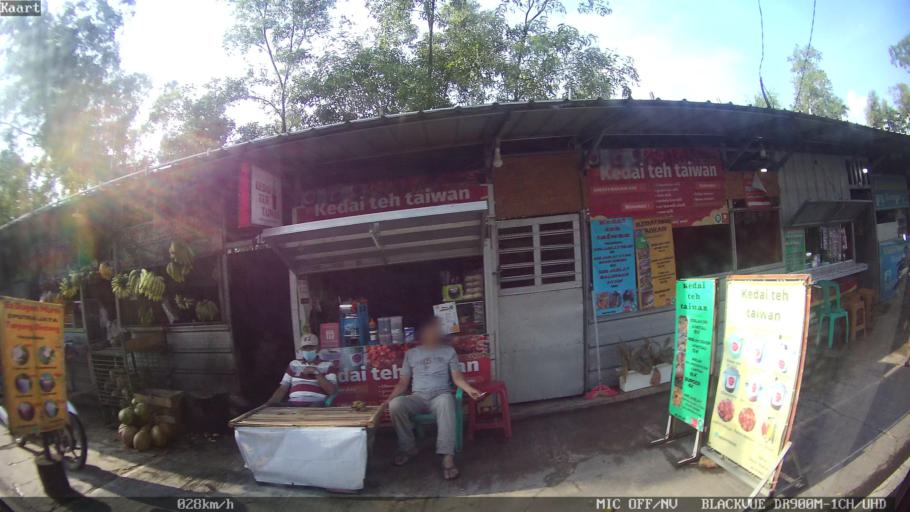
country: ID
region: Lampung
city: Kedaton
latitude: -5.3857
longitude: 105.3096
